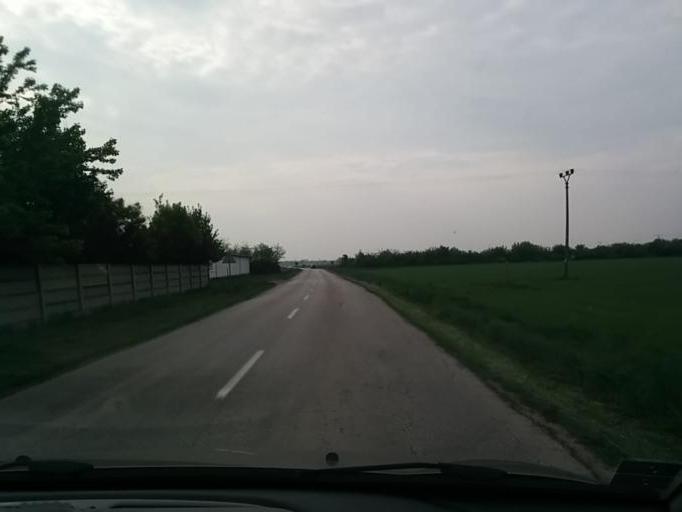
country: SK
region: Trnavsky
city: Sladkovicovo
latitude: 48.2164
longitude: 17.5973
